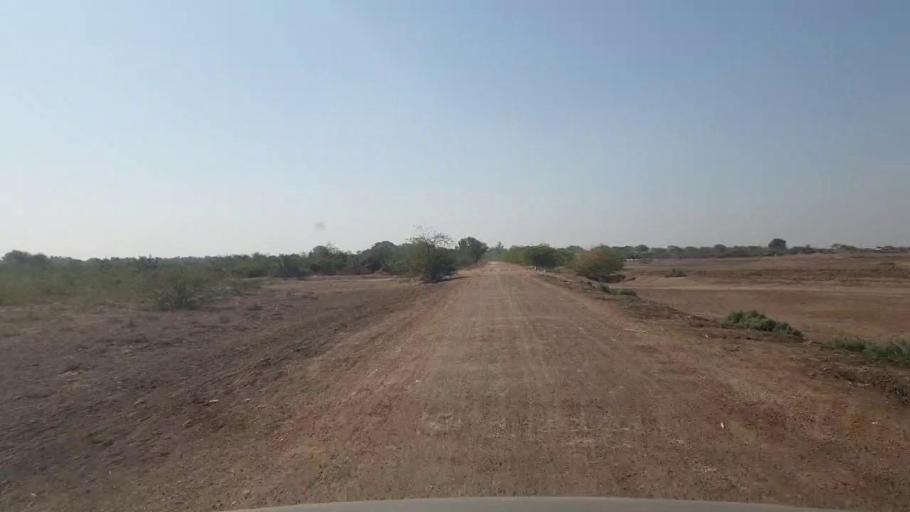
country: PK
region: Sindh
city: Digri
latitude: 25.2681
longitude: 69.2068
